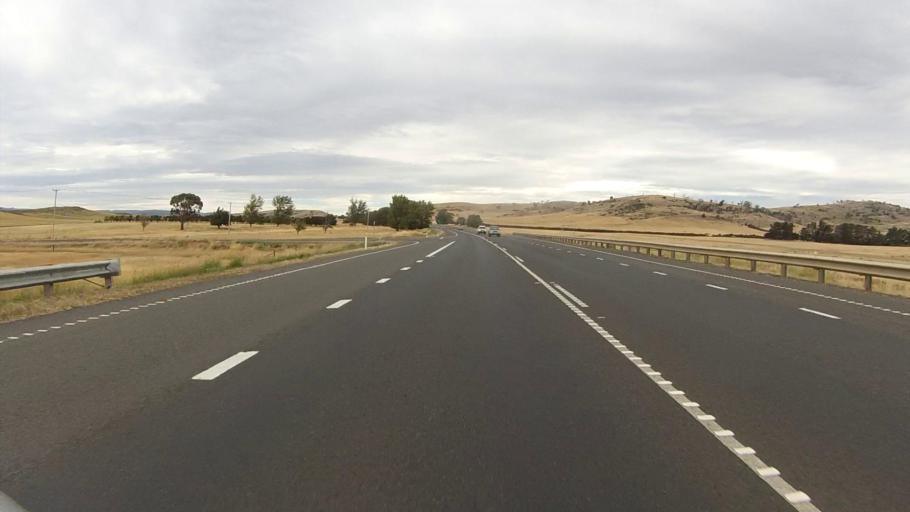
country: AU
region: Tasmania
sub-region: Brighton
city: Bridgewater
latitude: -42.3701
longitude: 147.3333
